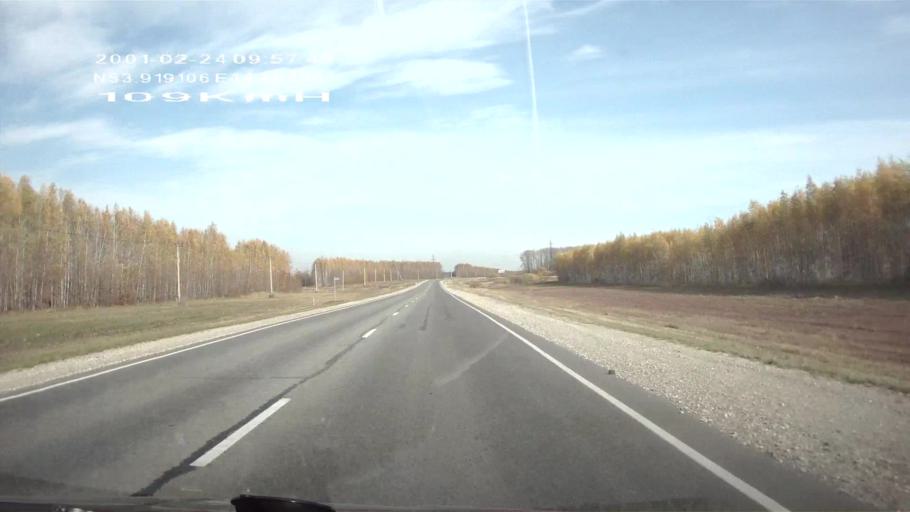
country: RU
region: Penza
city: Issa
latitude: 53.9196
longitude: 44.8641
